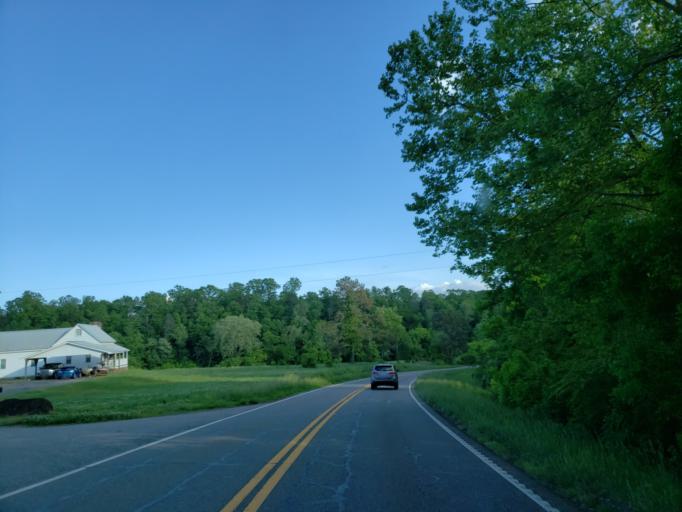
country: US
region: Georgia
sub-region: Cherokee County
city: Canton
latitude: 34.3297
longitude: -84.5620
